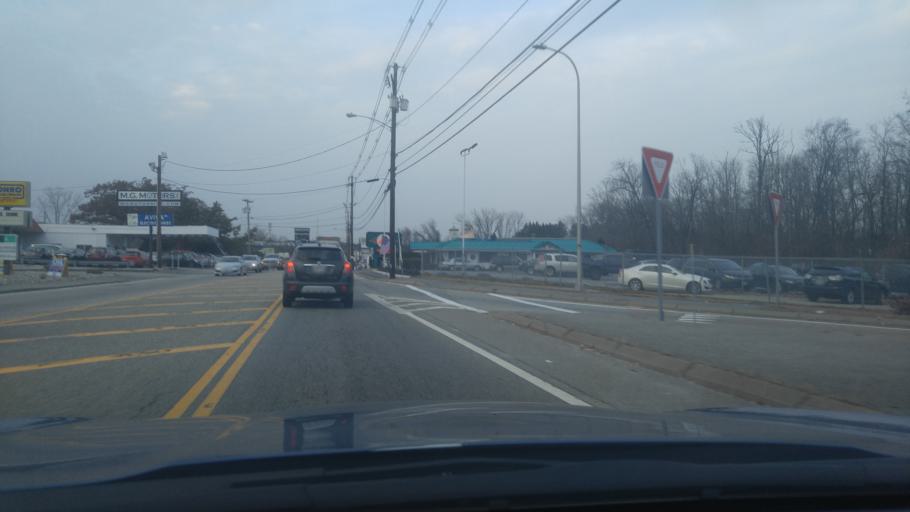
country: US
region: Rhode Island
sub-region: Providence County
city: Johnston
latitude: 41.8176
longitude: -71.4969
